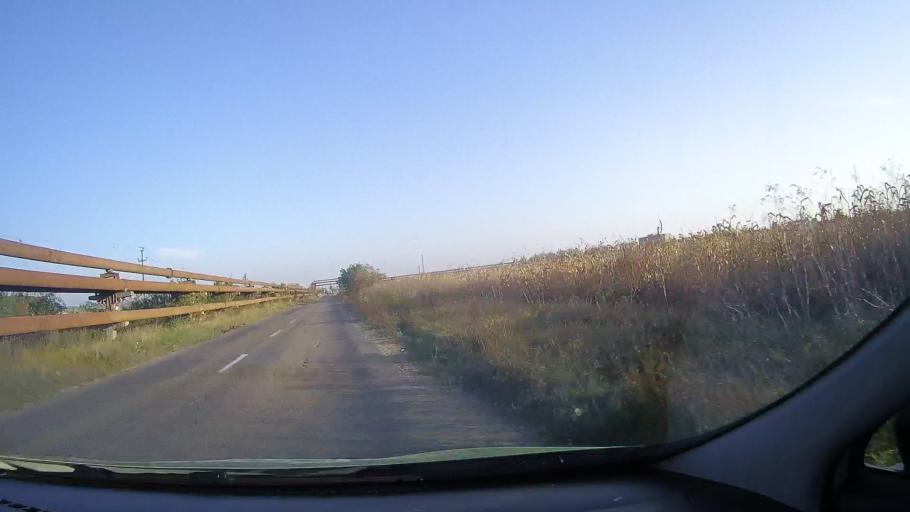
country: RO
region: Bihor
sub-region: Comuna Bors
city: Santion
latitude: 47.1097
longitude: 21.8653
